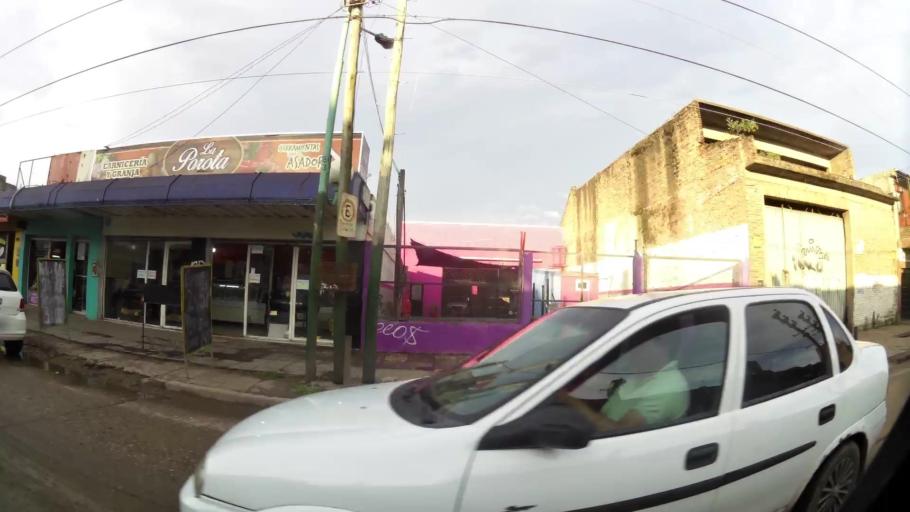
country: AR
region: Buenos Aires
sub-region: Partido de Almirante Brown
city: Adrogue
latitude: -34.7743
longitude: -58.3516
